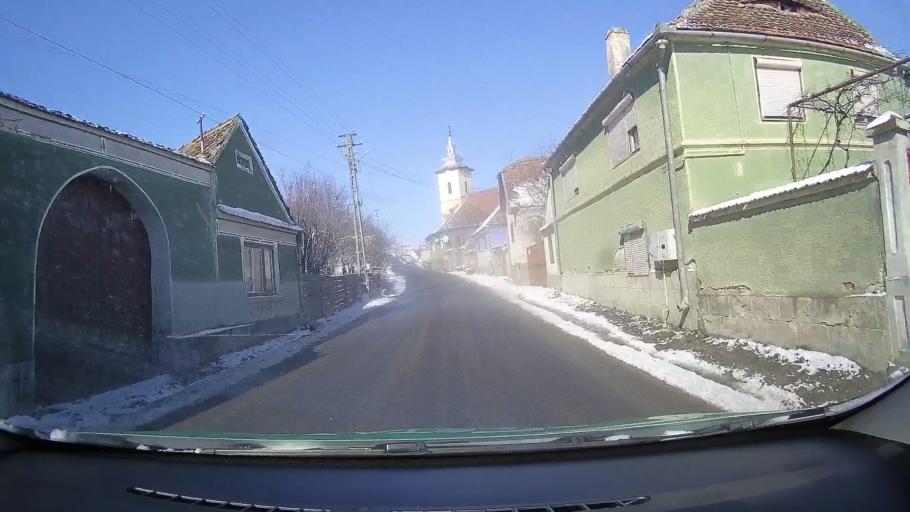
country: RO
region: Sibiu
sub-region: Comuna Avrig
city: Avrig
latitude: 45.7614
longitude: 24.3889
